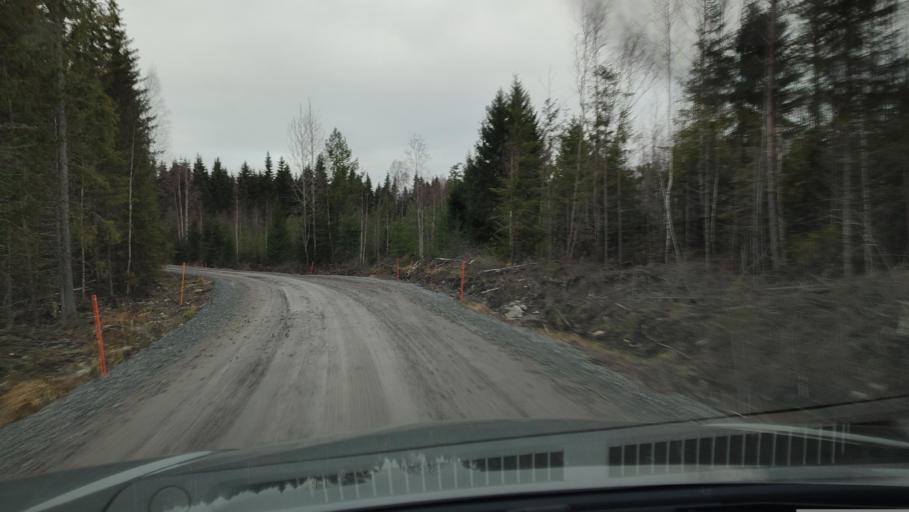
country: FI
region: Southern Ostrobothnia
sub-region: Suupohja
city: Karijoki
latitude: 62.1994
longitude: 21.5740
